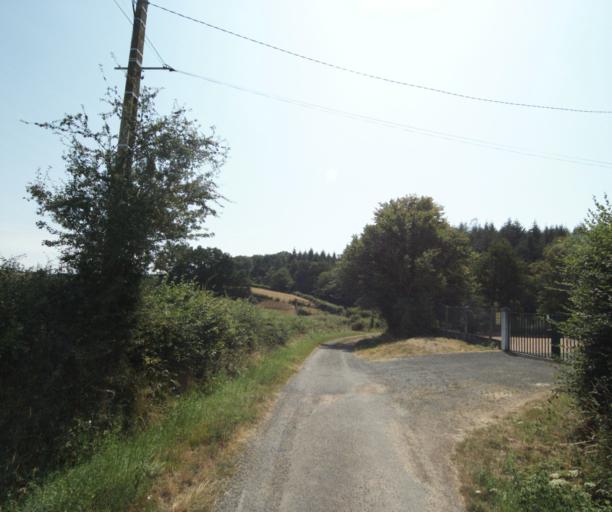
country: FR
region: Bourgogne
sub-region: Departement de Saone-et-Loire
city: Gueugnon
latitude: 46.5977
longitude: 4.0811
